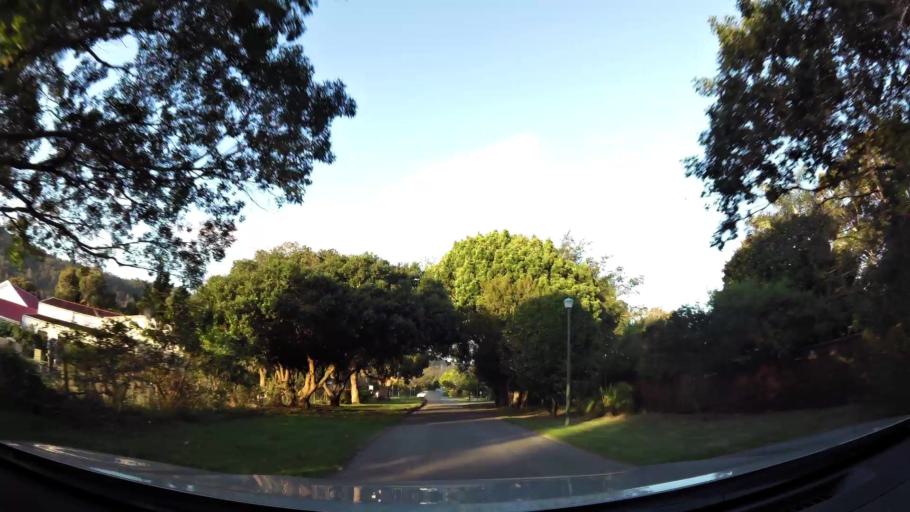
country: ZA
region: Western Cape
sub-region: Eden District Municipality
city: Knysna
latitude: -34.0198
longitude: 22.8076
